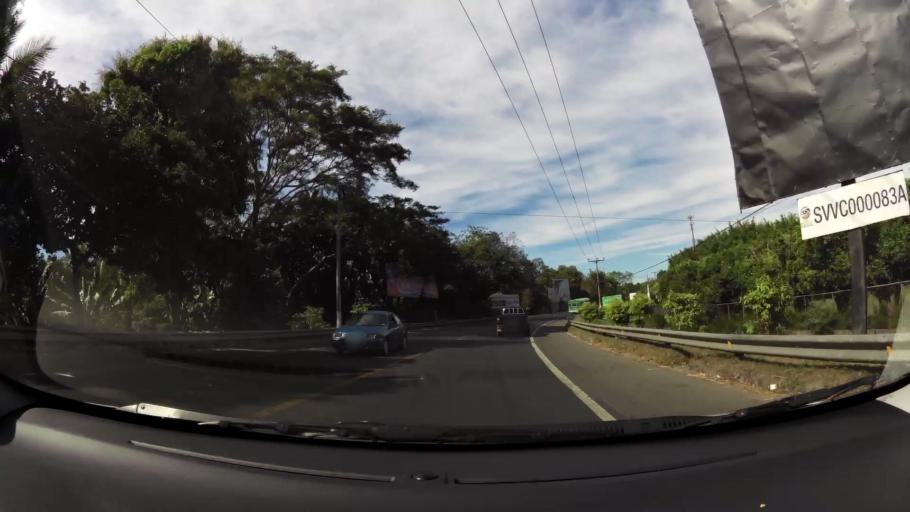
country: SV
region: San Salvador
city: Aguilares
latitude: 13.9414
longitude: -89.1898
